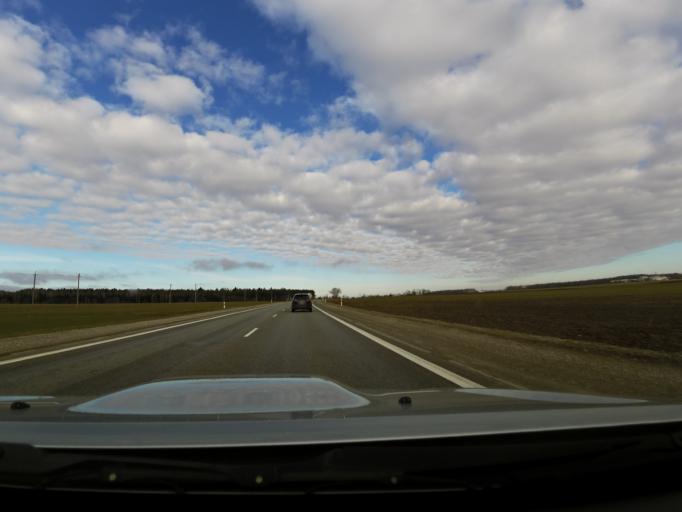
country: LT
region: Panevezys
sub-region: Panevezys City
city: Panevezys
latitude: 55.7661
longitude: 24.0697
